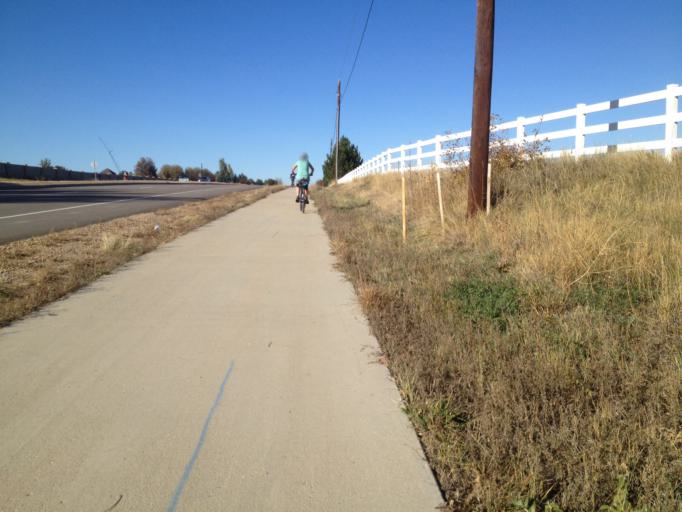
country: US
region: Colorado
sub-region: Boulder County
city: Niwot
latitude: 40.1310
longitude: -105.1497
